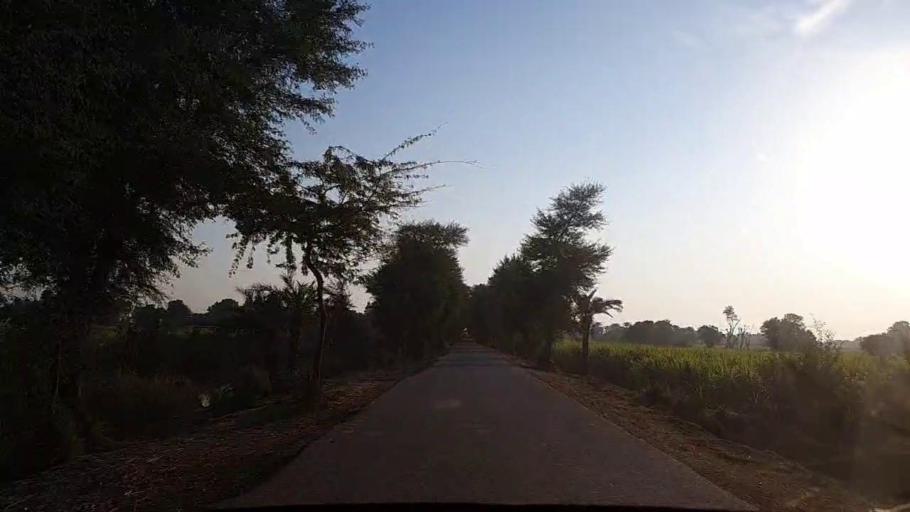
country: PK
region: Sindh
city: Sobhadero
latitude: 27.3917
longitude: 68.3847
